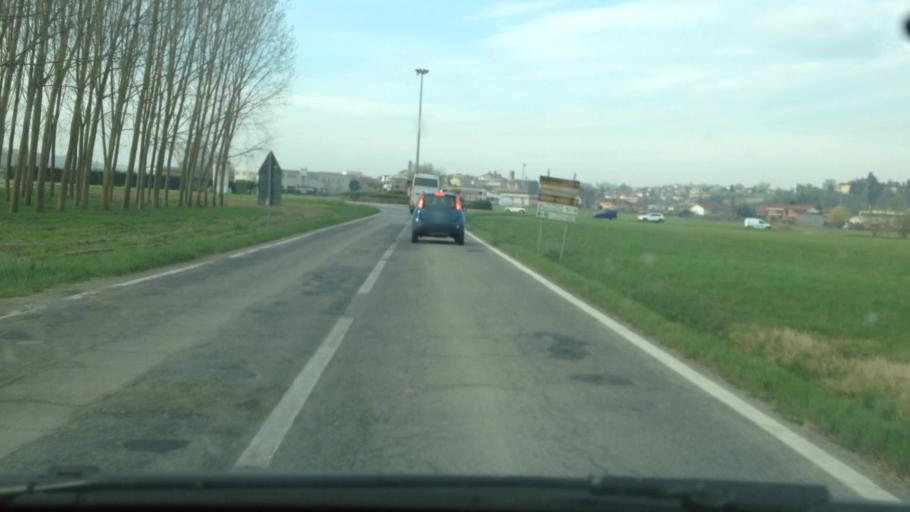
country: IT
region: Piedmont
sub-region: Provincia di Asti
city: San Damiano d'Asti
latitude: 44.8448
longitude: 8.0784
